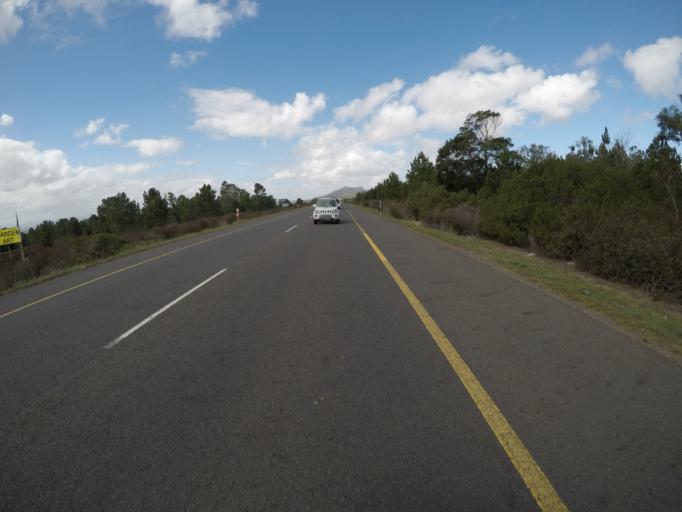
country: ZA
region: Western Cape
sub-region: Eden District Municipality
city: Riversdale
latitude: -34.2124
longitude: 21.5911
